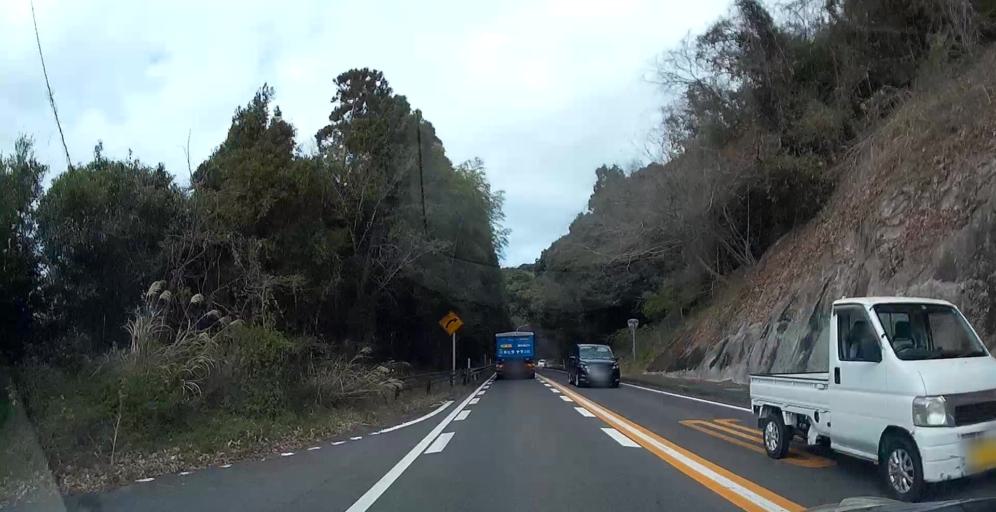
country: JP
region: Kumamoto
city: Minamata
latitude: 32.2310
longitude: 130.4408
